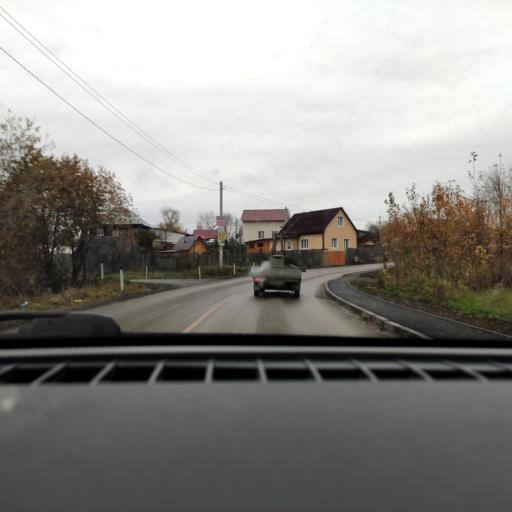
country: RU
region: Perm
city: Ferma
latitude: 57.9192
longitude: 56.2980
